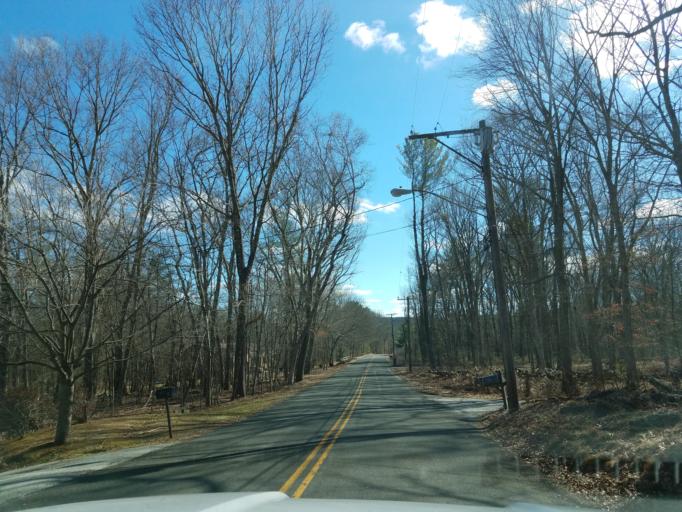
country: US
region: Massachusetts
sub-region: Worcester County
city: Webster
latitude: 42.0150
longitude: -71.8728
